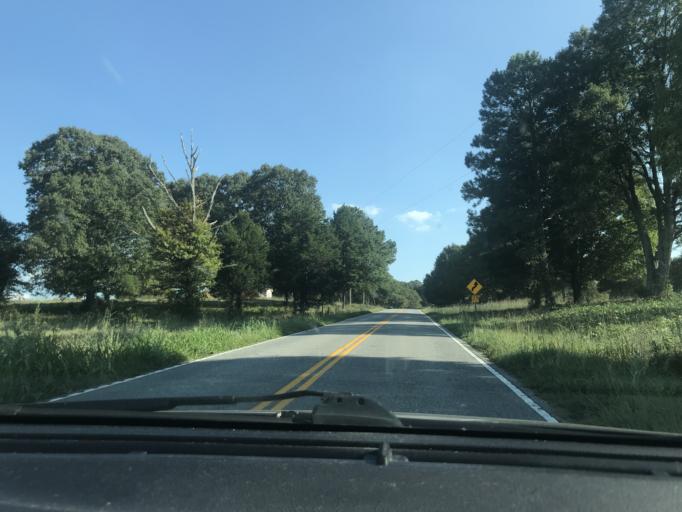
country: US
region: South Carolina
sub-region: Cherokee County
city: Gaffney
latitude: 35.1168
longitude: -81.6792
